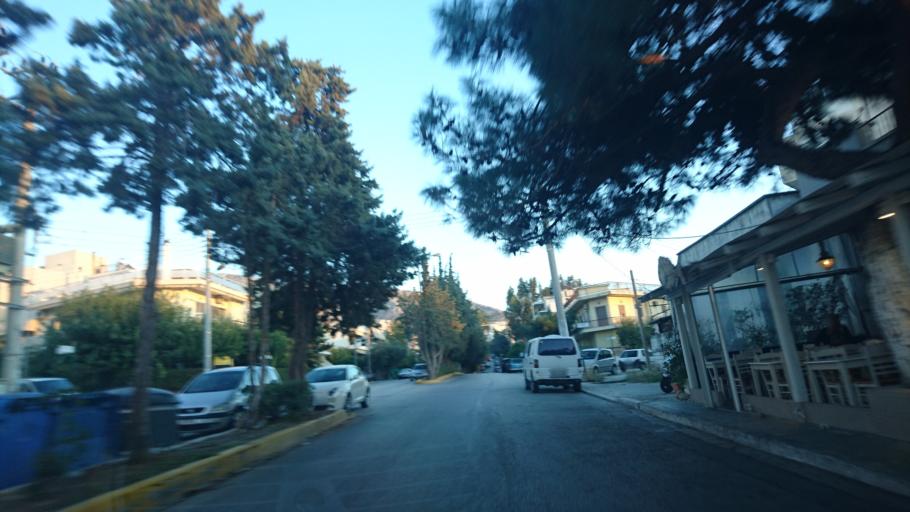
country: GR
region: Attica
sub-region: Nomarchia Athinas
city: Ilioupoli
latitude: 37.9301
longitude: 23.7518
